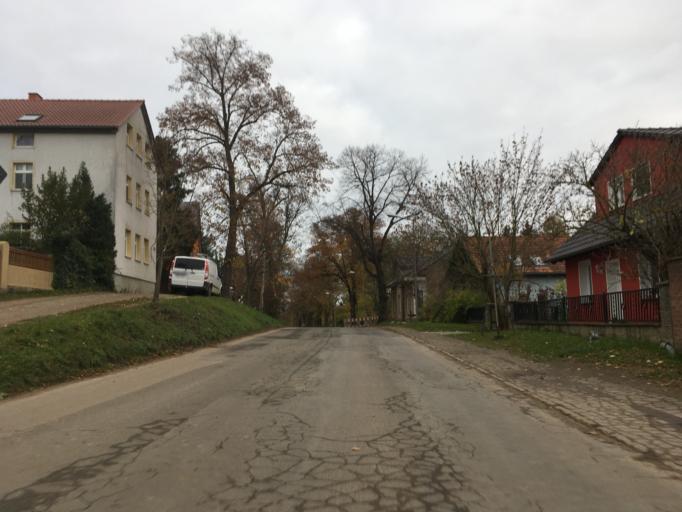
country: DE
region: Brandenburg
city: Frankfurt (Oder)
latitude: 52.3131
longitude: 14.5418
